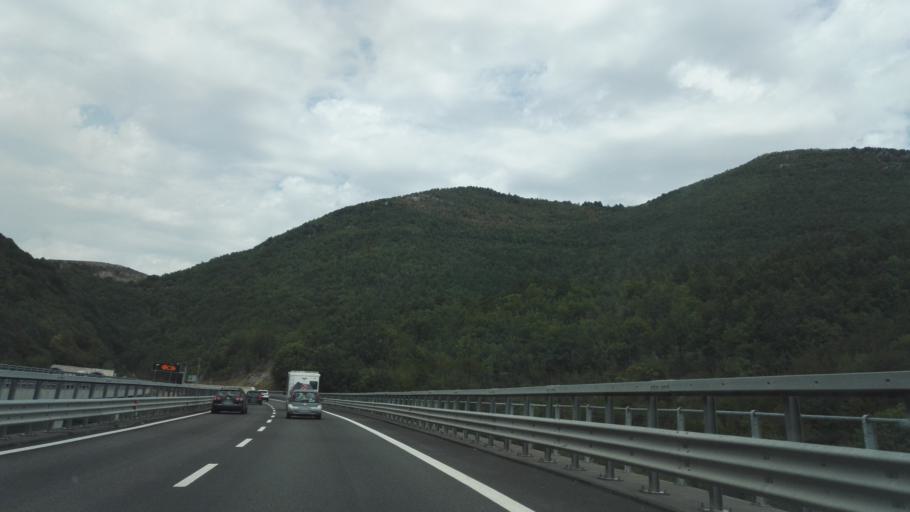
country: IT
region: Basilicate
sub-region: Provincia di Potenza
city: Castelluccio Superiore
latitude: 39.9896
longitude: 15.9334
